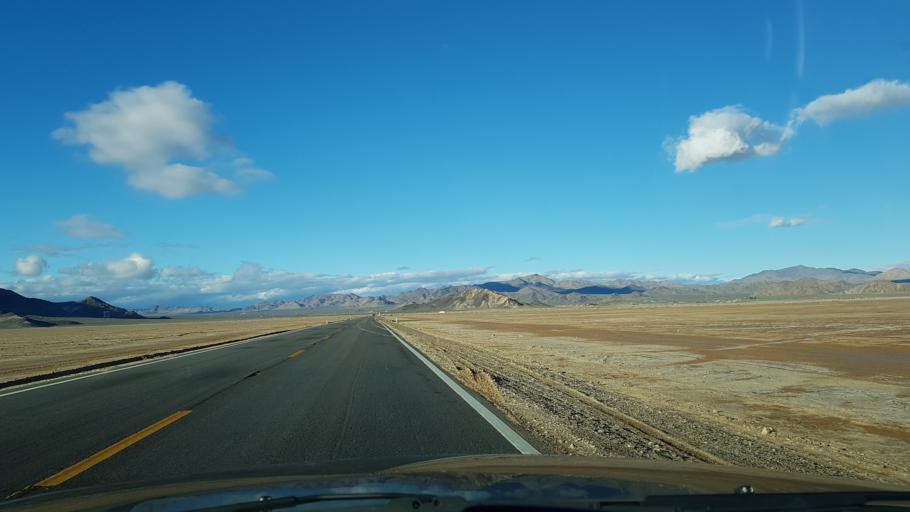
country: US
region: California
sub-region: San Bernardino County
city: Lucerne Valley
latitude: 34.5085
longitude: -116.9453
